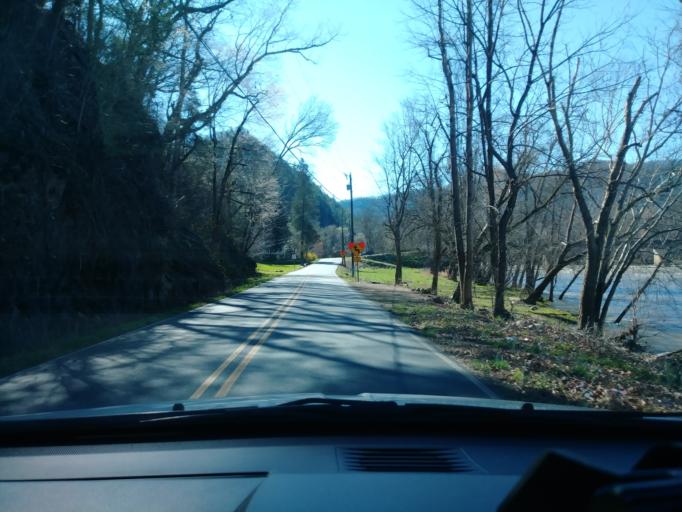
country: US
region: North Carolina
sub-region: Madison County
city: Marshall
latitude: 35.8958
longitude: -82.8231
